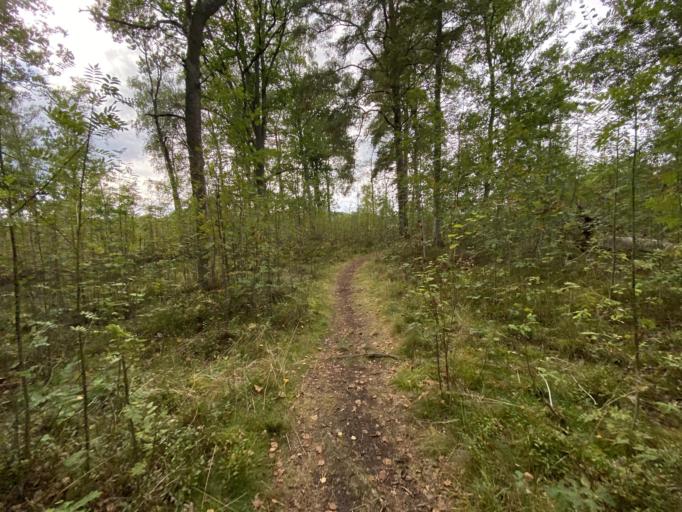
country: SE
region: Skane
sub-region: Hassleholms Kommun
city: Hastveda
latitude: 56.3611
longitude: 13.8867
